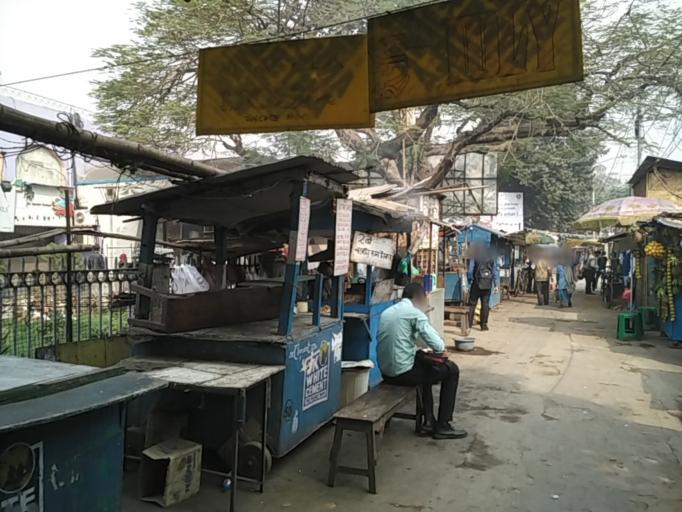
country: IN
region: West Bengal
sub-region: Kolkata
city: Kolkata
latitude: 22.4942
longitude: 88.3453
